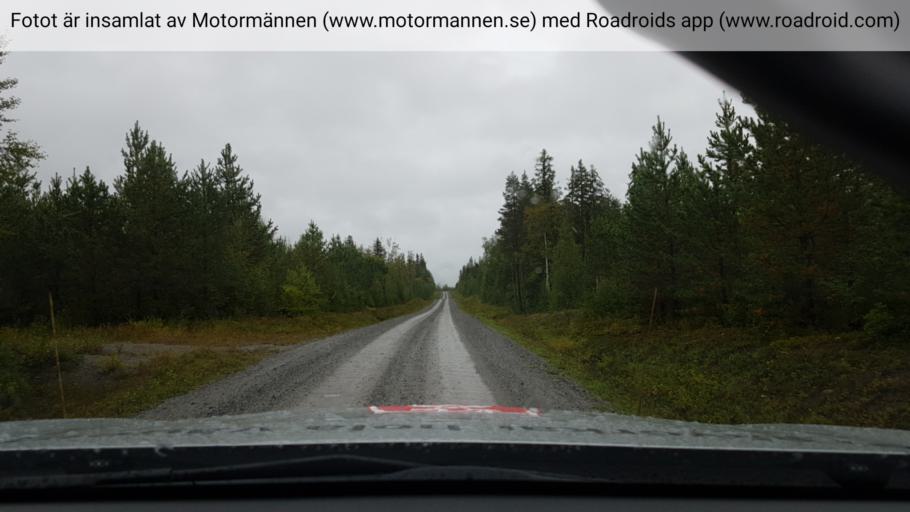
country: SE
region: Vaesterbotten
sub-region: Asele Kommun
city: Asele
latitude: 64.0144
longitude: 17.6293
